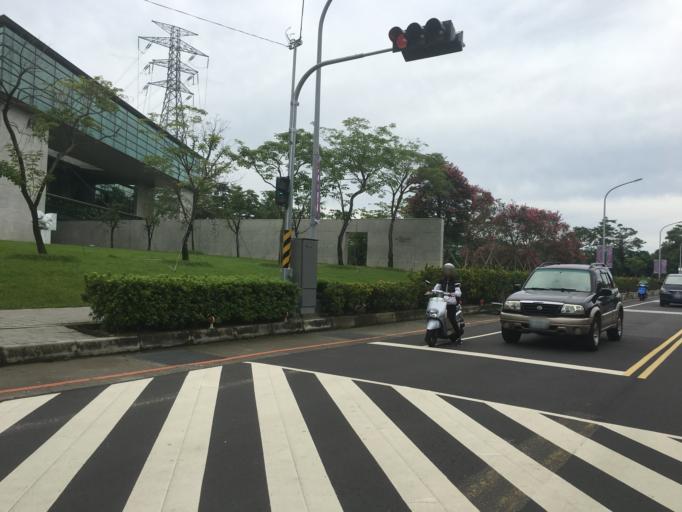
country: TW
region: Taiwan
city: Zhongxing New Village
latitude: 24.0472
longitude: 120.6873
